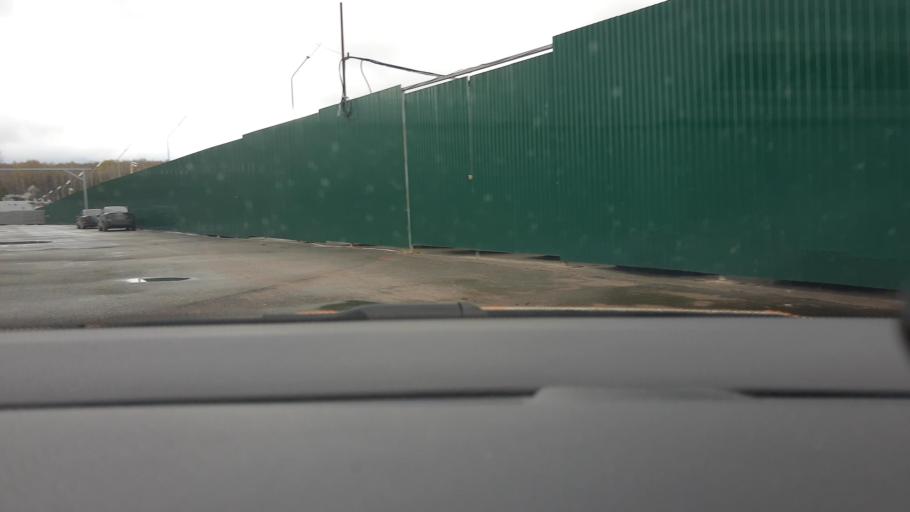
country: RU
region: Moscow
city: Lianozovo
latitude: 55.9101
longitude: 37.5951
